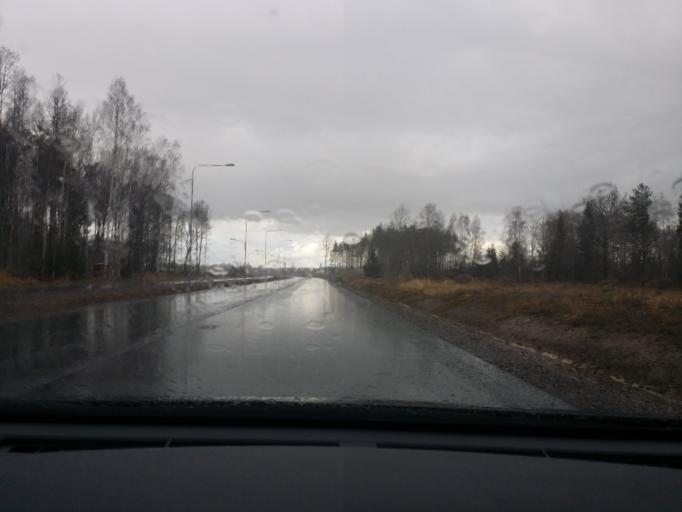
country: SE
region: Soedermanland
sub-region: Eskilstuna Kommun
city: Arla
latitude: 59.3585
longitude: 16.7003
